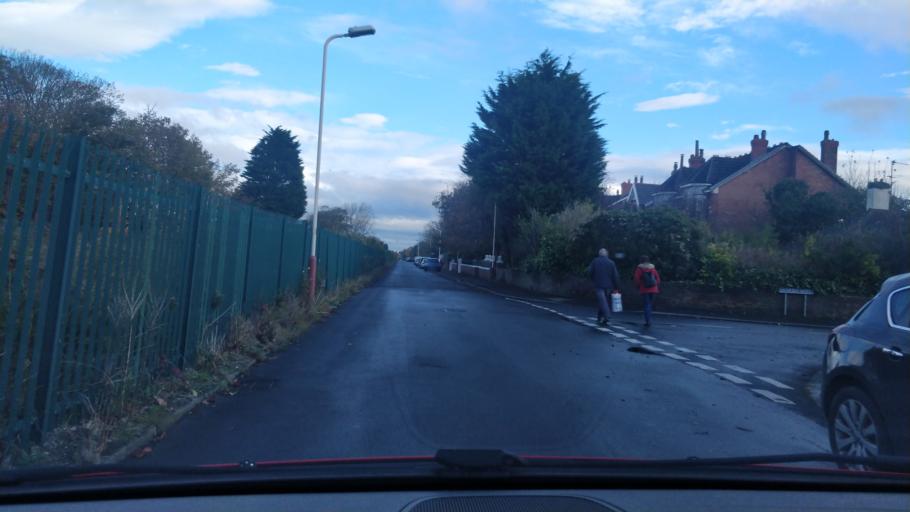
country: GB
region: England
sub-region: Sefton
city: Southport
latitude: 53.6253
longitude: -3.0219
